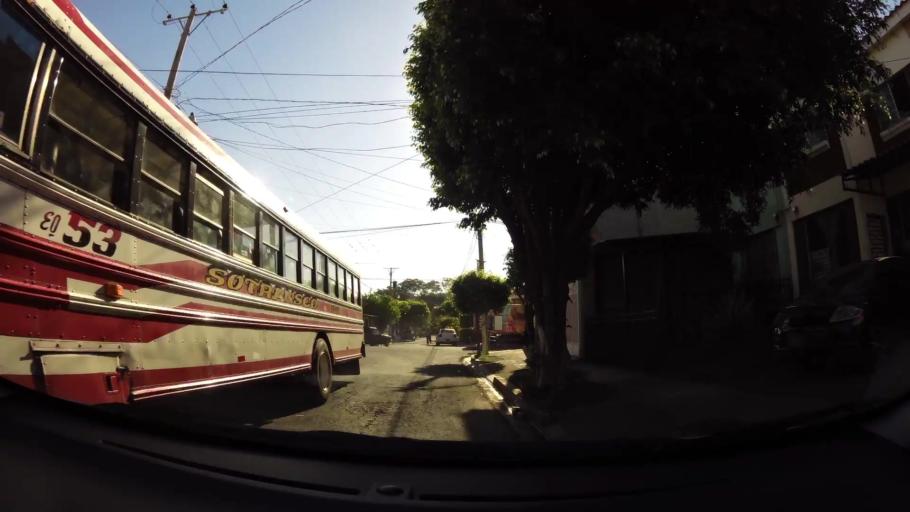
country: SV
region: Sonsonate
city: Sonzacate
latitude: 13.7289
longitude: -89.7110
